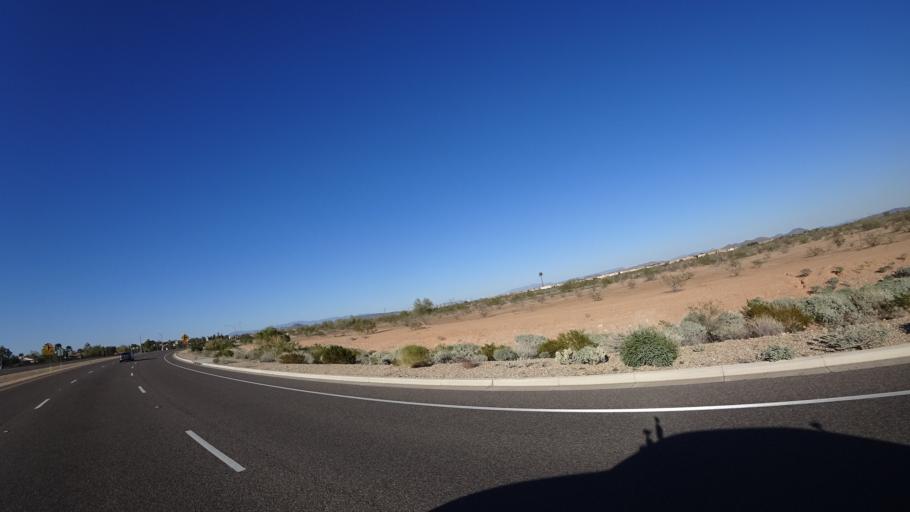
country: US
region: Arizona
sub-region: Maricopa County
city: Sun City West
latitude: 33.6871
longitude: -112.3332
